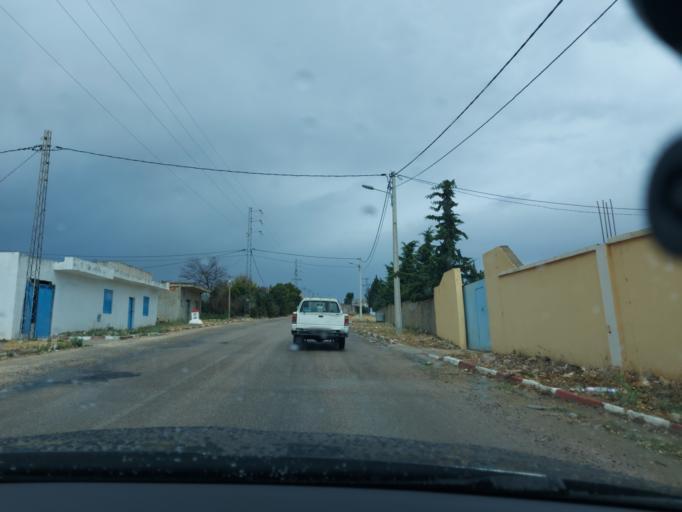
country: TN
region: Silyanah
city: Maktar
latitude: 35.8528
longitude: 9.2142
